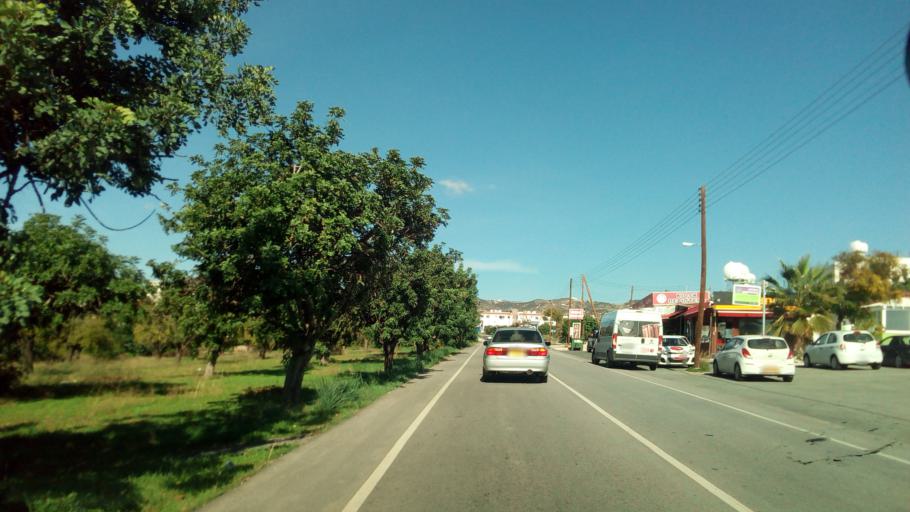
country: CY
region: Pafos
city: Mesogi
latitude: 34.8083
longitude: 32.4501
